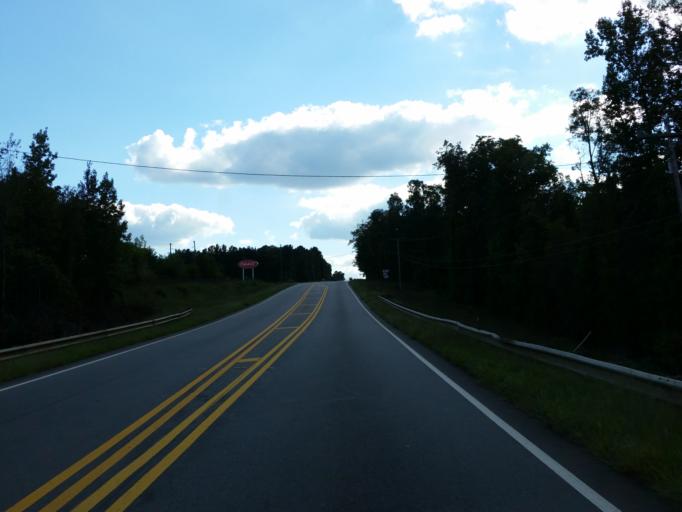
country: US
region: Georgia
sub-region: Butts County
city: Jackson
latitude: 33.2016
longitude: -84.0650
